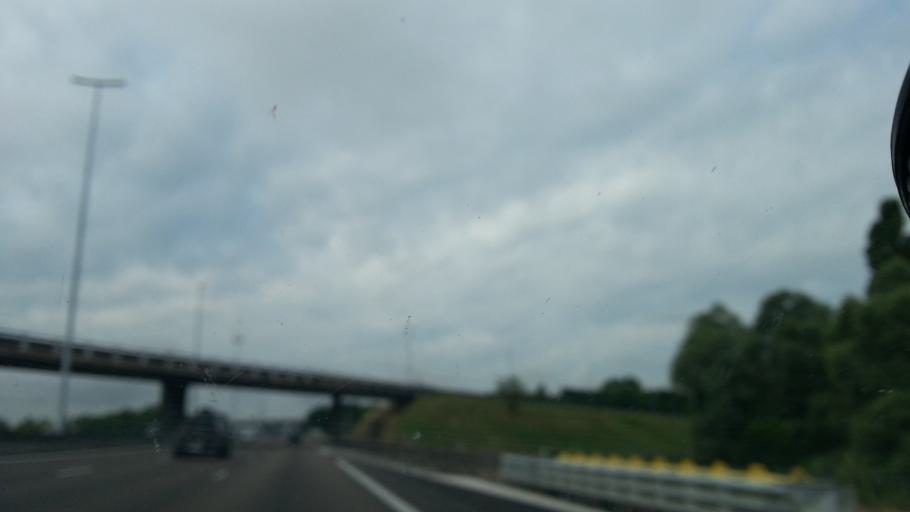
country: FR
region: Bourgogne
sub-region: Departement de la Cote-d'Or
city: Beaune
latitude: 47.0315
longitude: 4.8773
